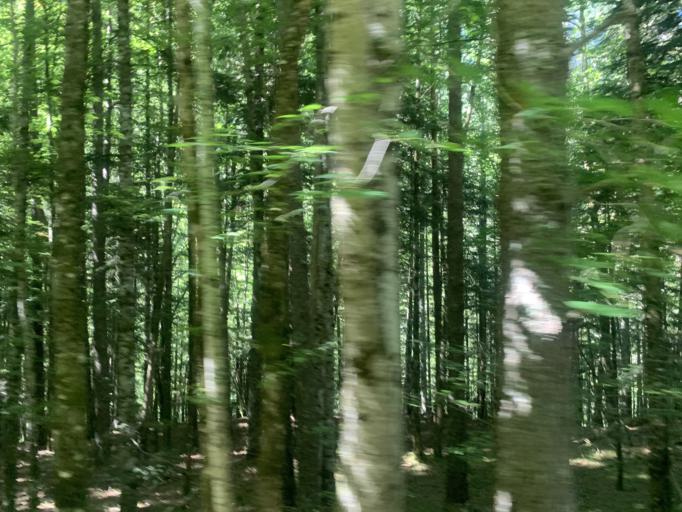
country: ES
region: Aragon
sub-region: Provincia de Huesca
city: Broto
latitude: 42.6512
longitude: -0.0709
